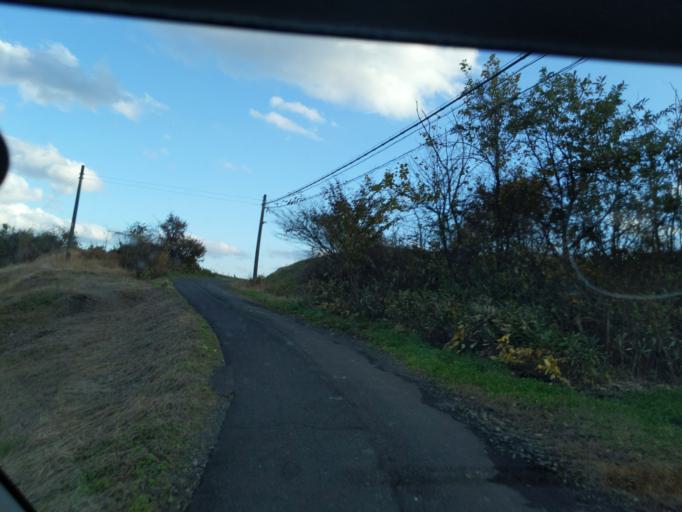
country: JP
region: Iwate
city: Mizusawa
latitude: 39.0993
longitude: 141.0387
